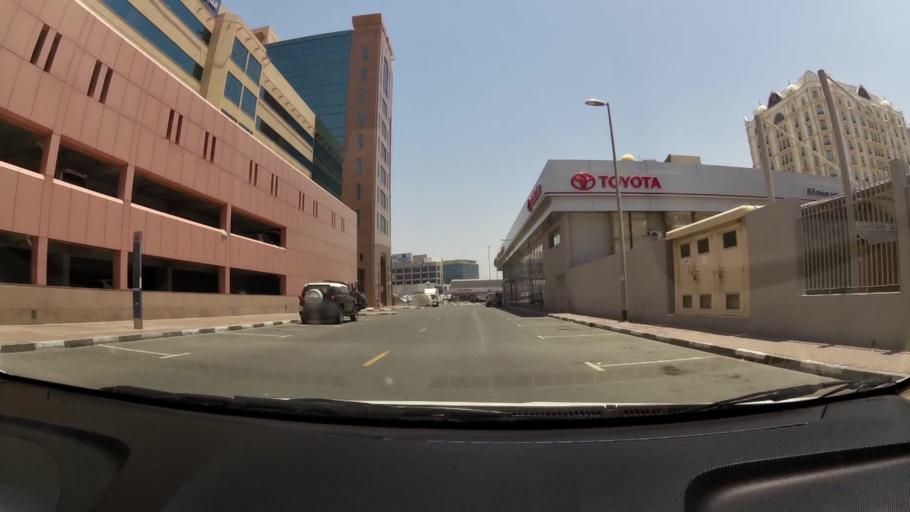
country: AE
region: Ash Shariqah
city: Sharjah
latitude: 25.2563
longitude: 55.3315
